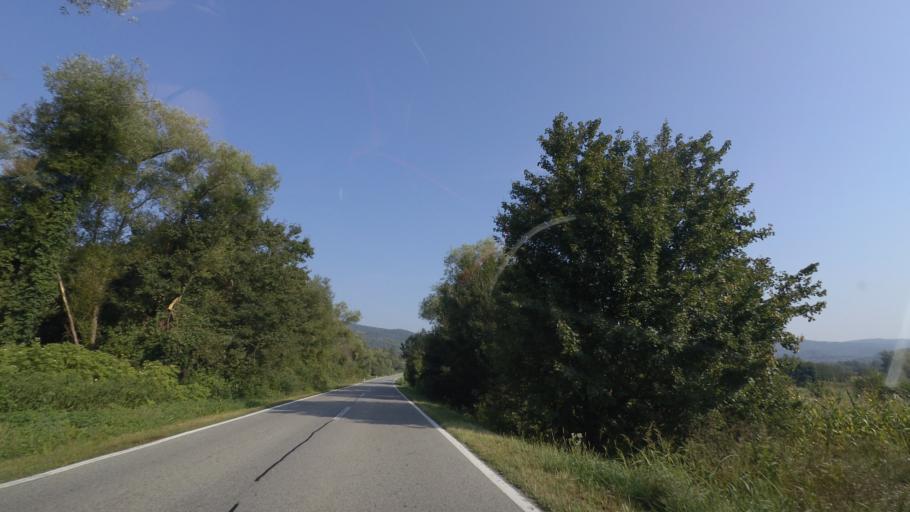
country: HR
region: Brodsko-Posavska
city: Resetari
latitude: 45.4045
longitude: 17.5012
